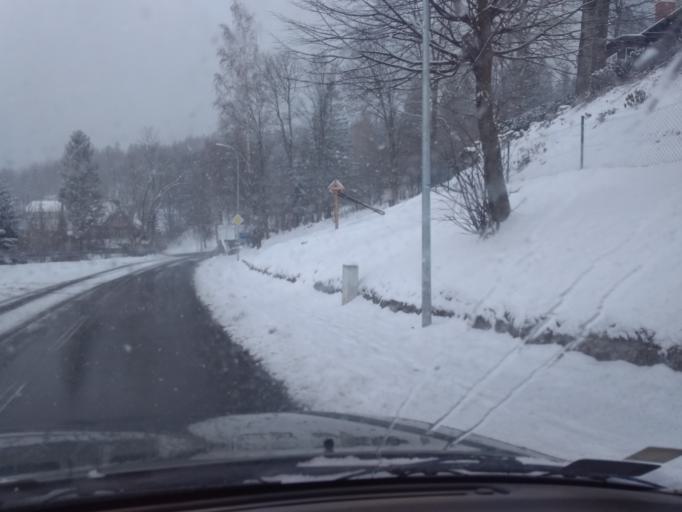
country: PL
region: Lower Silesian Voivodeship
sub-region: Powiat jeleniogorski
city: Karpacz
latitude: 50.7758
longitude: 15.7268
